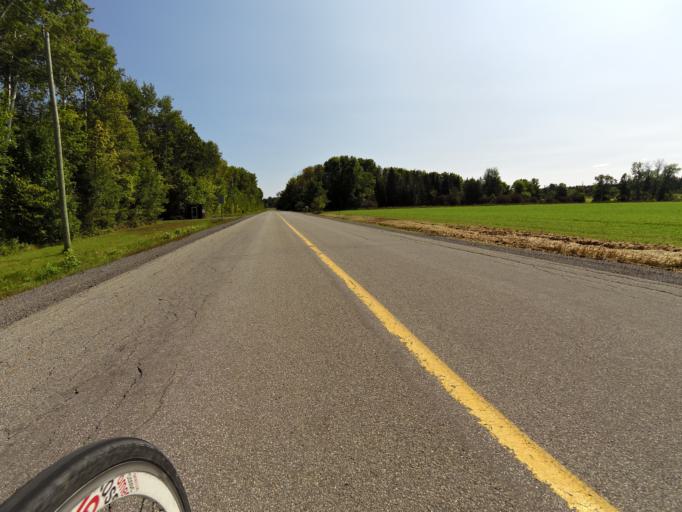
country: CA
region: Ontario
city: Arnprior
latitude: 45.5096
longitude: -76.1633
